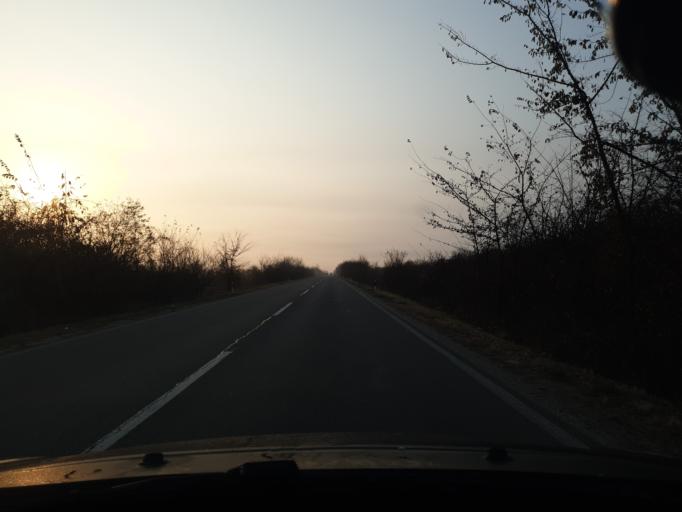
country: RS
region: Central Serbia
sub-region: Jablanicki Okrug
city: Leskovac
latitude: 42.9645
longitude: 21.9800
